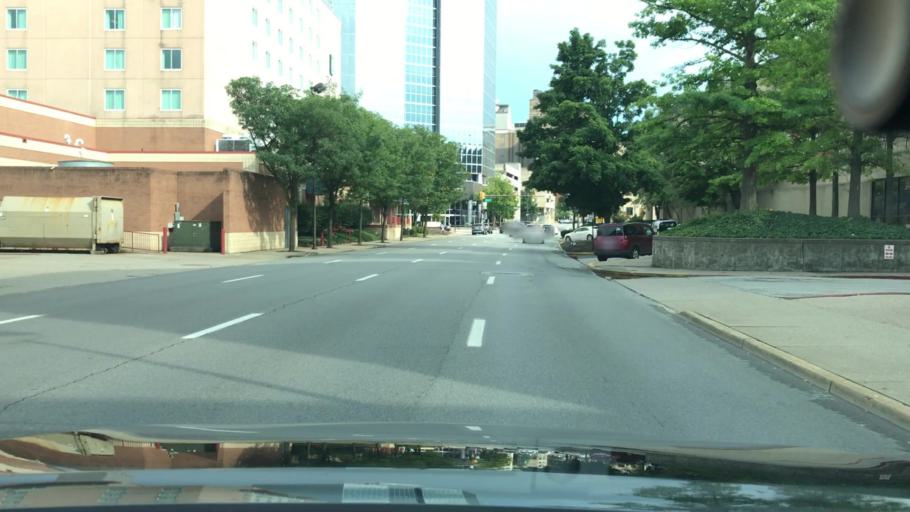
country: US
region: West Virginia
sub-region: Kanawha County
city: Charleston
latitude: 38.3543
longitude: -81.6364
